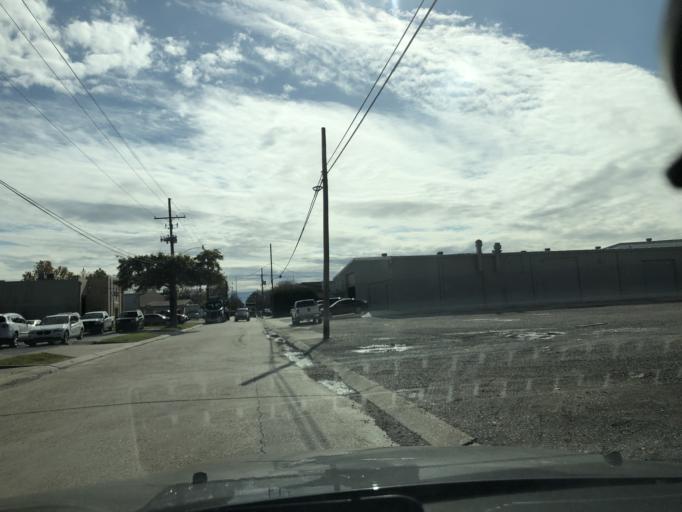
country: US
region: Louisiana
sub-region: Jefferson Parish
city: Metairie
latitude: 29.9968
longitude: -90.1609
